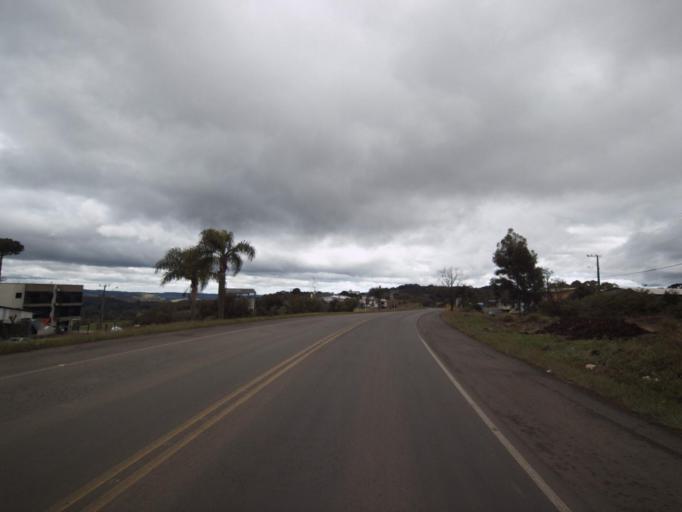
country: BR
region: Santa Catarina
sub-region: Concordia
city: Concordia
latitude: -27.2435
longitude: -51.9515
